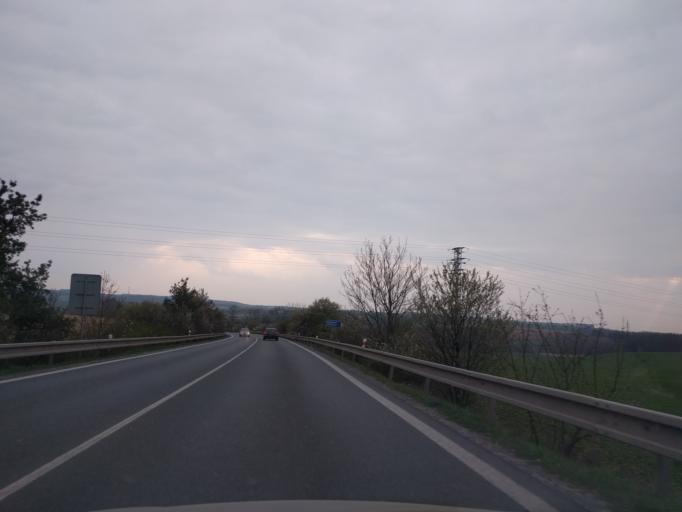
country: CZ
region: Central Bohemia
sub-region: Okres Praha-Vychod
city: Ricany
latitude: 49.9854
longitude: 14.6390
